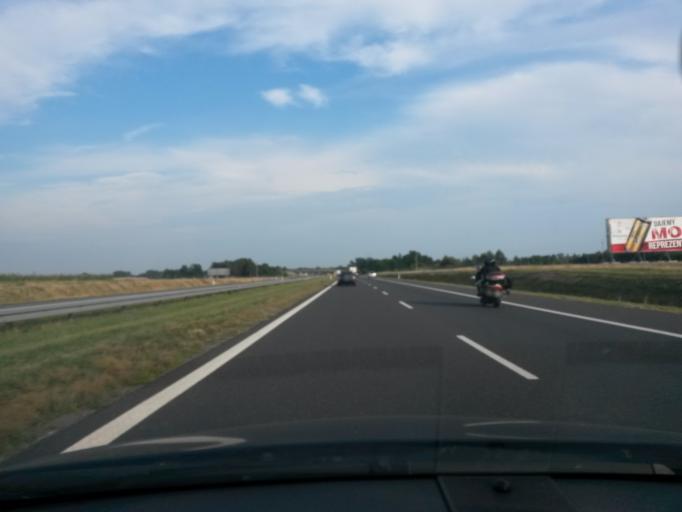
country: PL
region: Lodz Voivodeship
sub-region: Powiat poddebicki
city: Wartkowice
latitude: 51.9774
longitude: 19.0774
